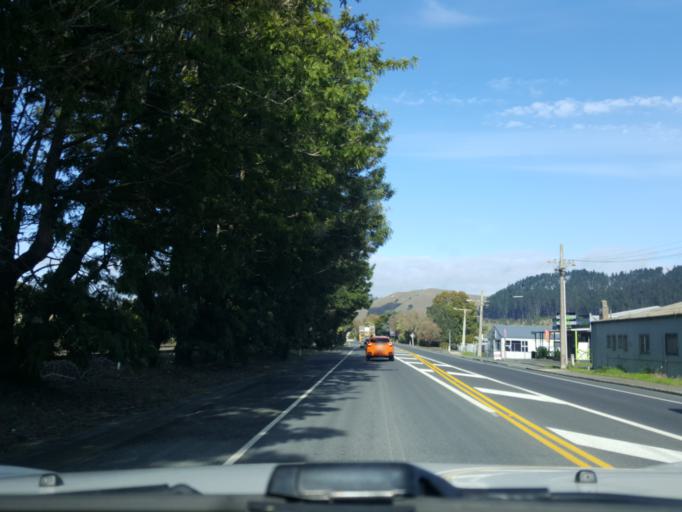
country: NZ
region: Waikato
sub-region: Waikato District
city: Ngaruawahia
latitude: -37.5786
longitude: 175.1596
